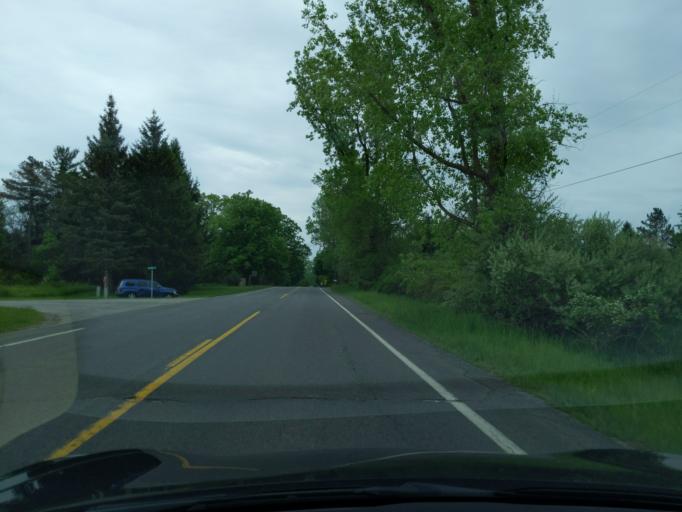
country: US
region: Michigan
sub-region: Ingham County
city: Haslett
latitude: 42.7406
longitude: -84.3635
